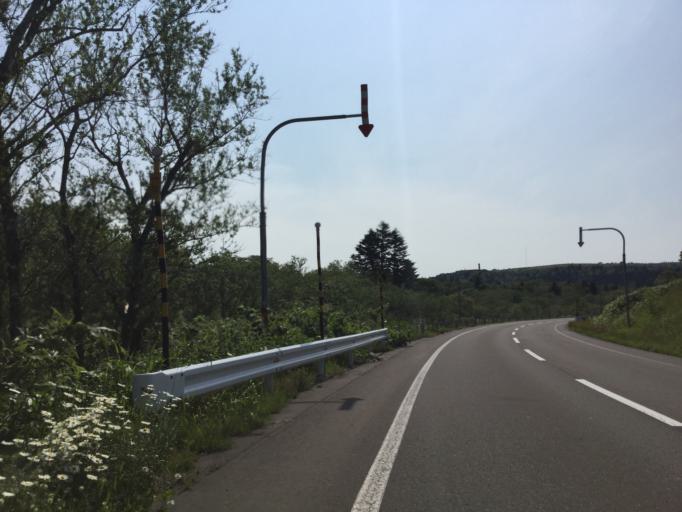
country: JP
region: Hokkaido
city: Makubetsu
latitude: 45.4067
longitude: 141.9667
